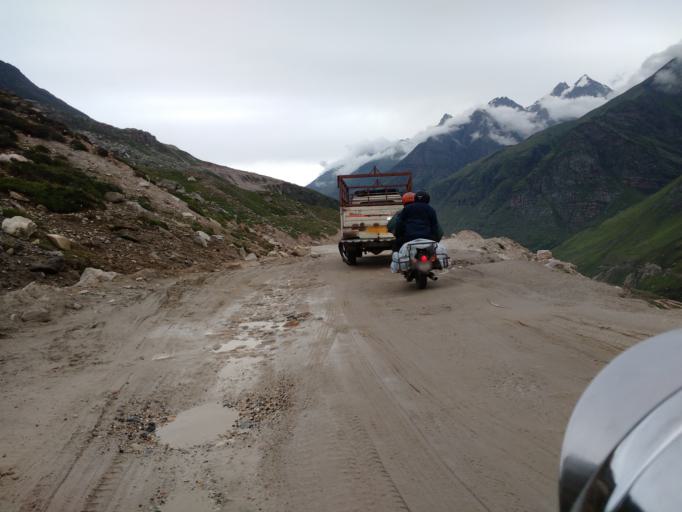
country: IN
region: Himachal Pradesh
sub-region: Kulu
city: Manali
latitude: 32.3802
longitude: 77.2660
